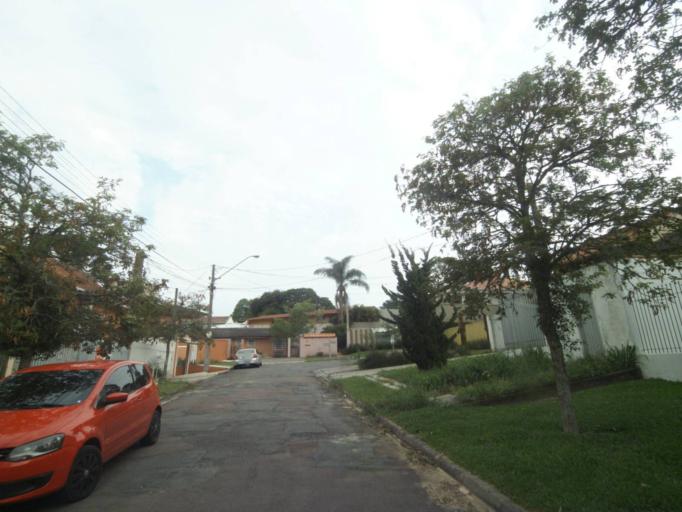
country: BR
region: Parana
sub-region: Curitiba
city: Curitiba
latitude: -25.3991
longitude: -49.2795
